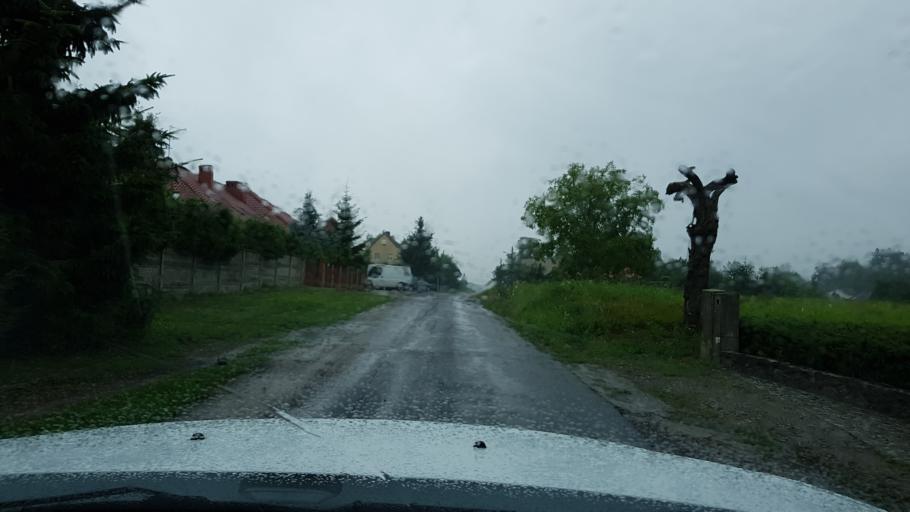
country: PL
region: West Pomeranian Voivodeship
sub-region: Powiat gryfinski
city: Chojna
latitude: 52.9531
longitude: 14.4260
